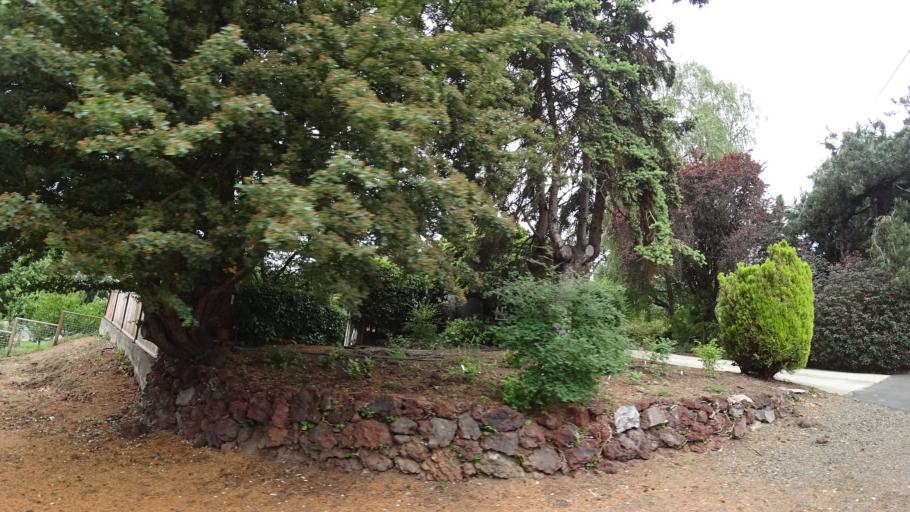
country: US
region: Oregon
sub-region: Multnomah County
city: Portland
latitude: 45.4819
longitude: -122.6993
